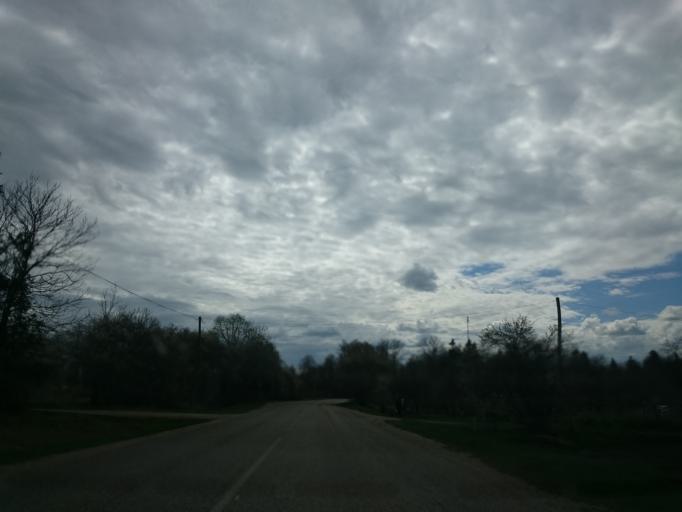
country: LV
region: Aizpute
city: Aizpute
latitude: 56.7388
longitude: 21.6080
